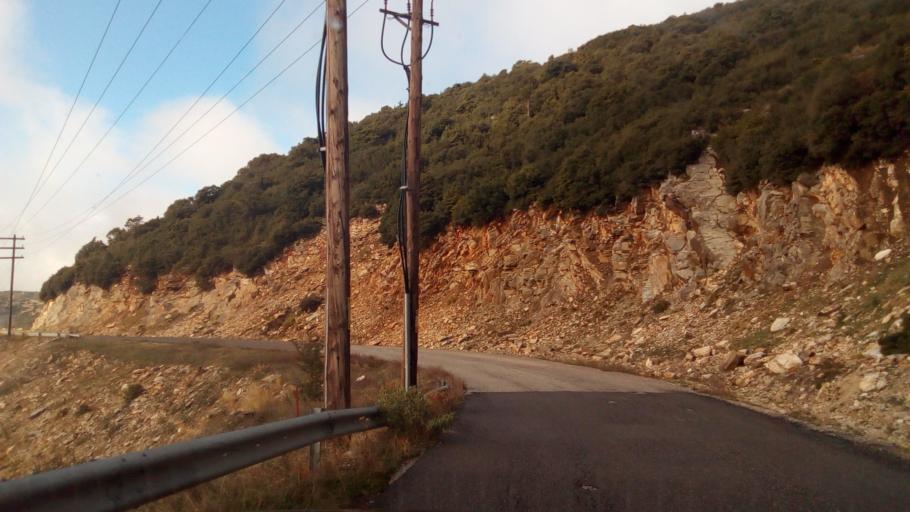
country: GR
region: West Greece
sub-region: Nomos Aitolias kai Akarnanias
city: Thermo
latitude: 38.5861
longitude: 21.7674
